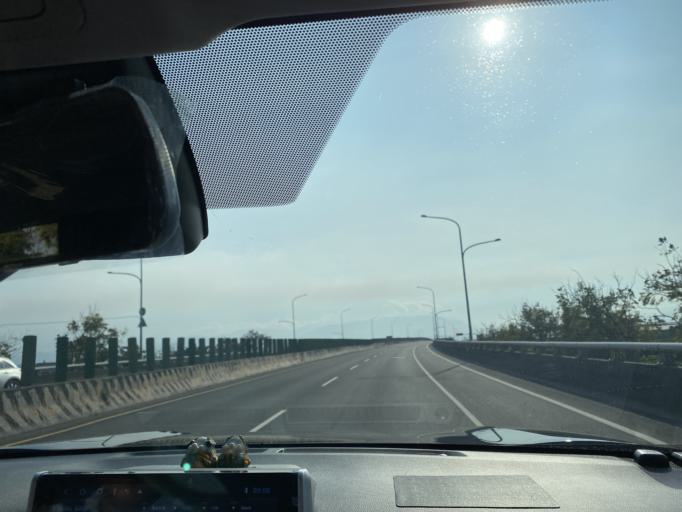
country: TW
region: Taiwan
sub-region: Yunlin
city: Douliu
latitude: 23.7161
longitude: 120.5531
